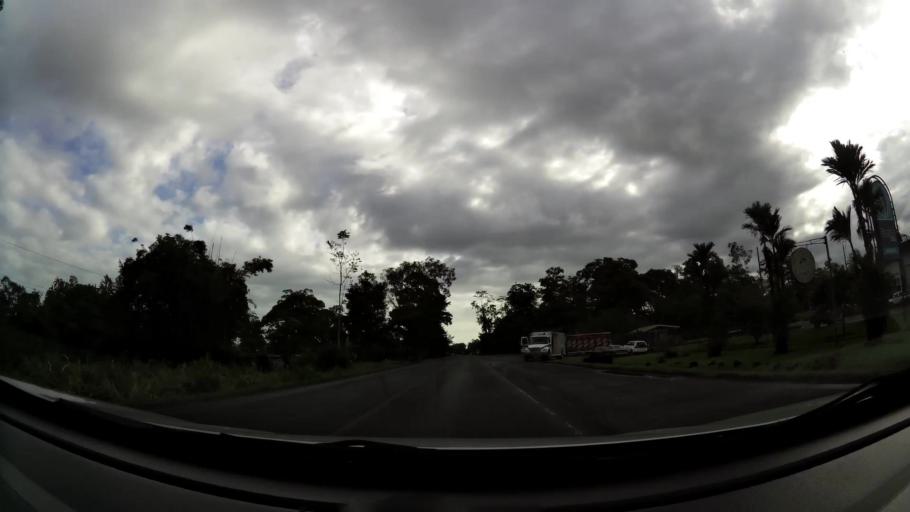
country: CR
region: Limon
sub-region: Canton de Pococi
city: Guapiles
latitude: 10.2034
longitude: -83.7722
